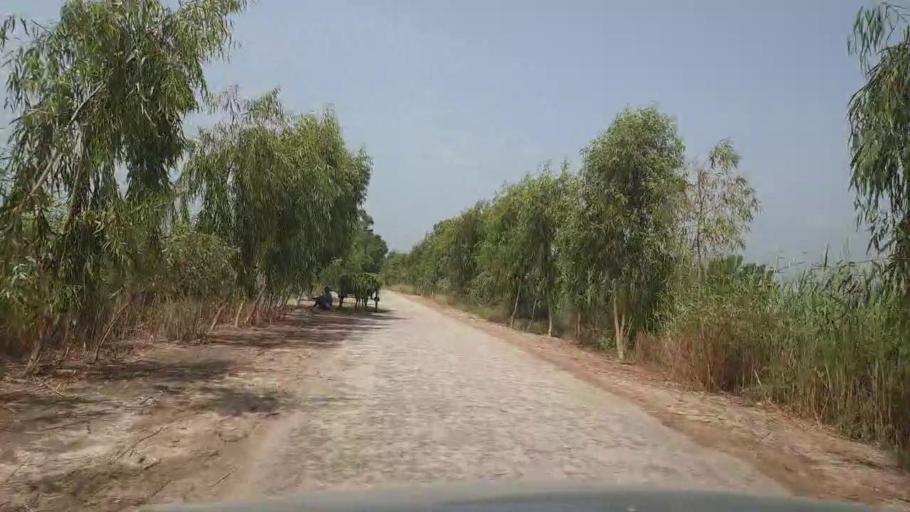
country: PK
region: Sindh
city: Garhi Yasin
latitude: 27.9467
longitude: 68.3708
